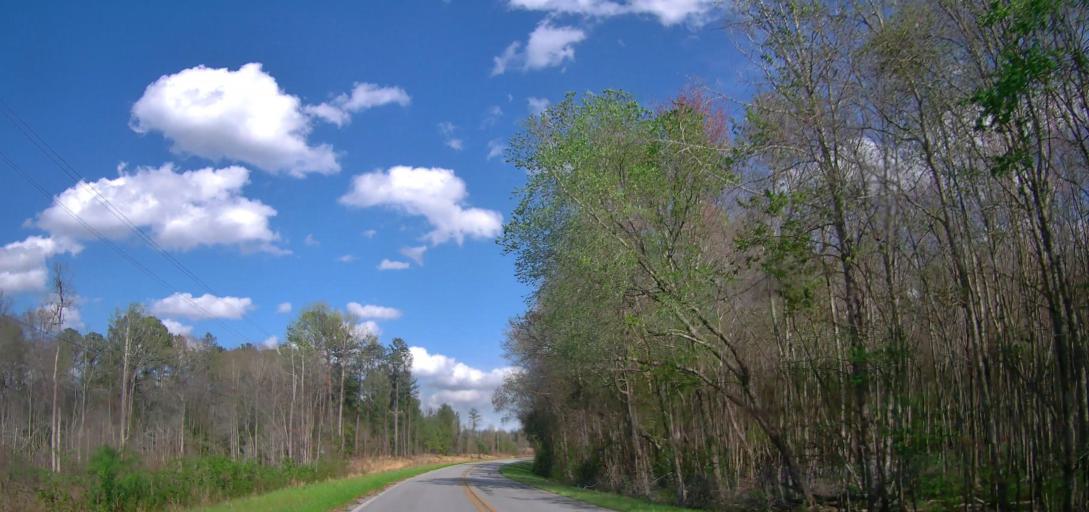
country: US
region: Georgia
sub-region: Wilkinson County
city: Gordon
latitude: 32.8261
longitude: -83.4196
